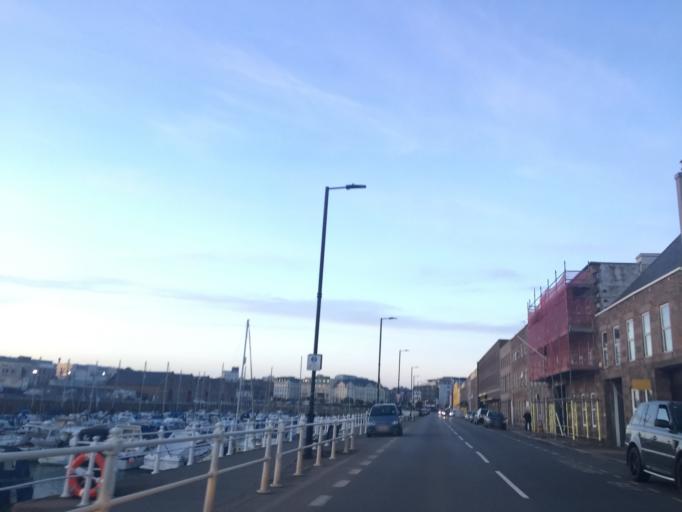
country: JE
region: St Helier
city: Saint Helier
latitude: 49.1792
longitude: -2.1097
